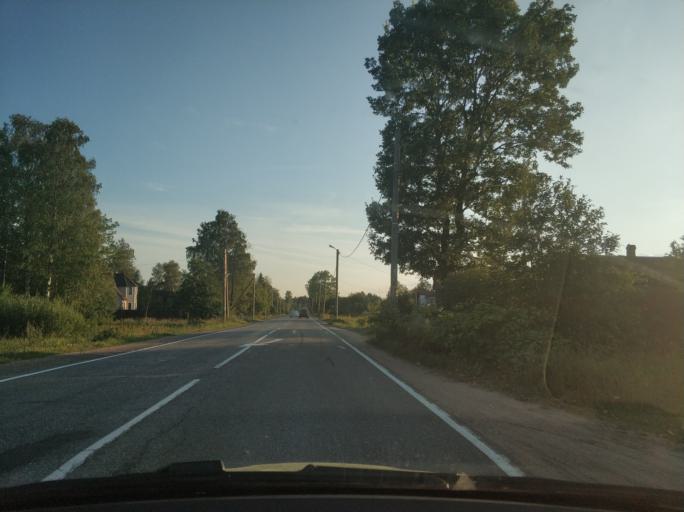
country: RU
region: Leningrad
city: Borisova Griva
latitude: 60.0947
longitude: 30.9659
